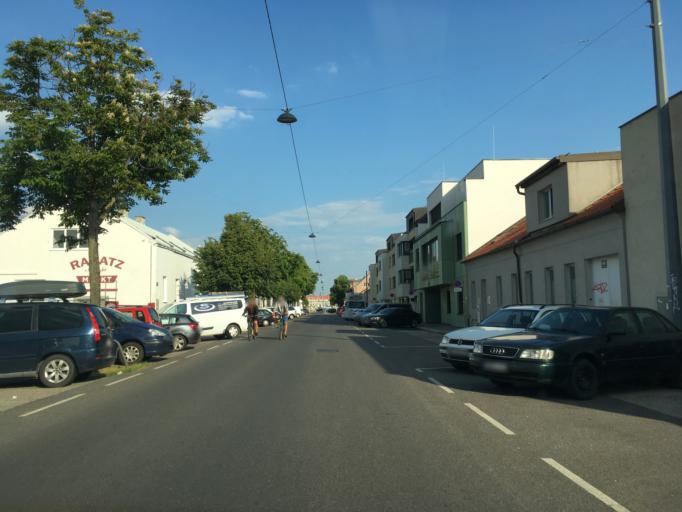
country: AT
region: Lower Austria
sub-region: Politischer Bezirk Modling
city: Vosendorf
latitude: 48.1393
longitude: 16.3211
